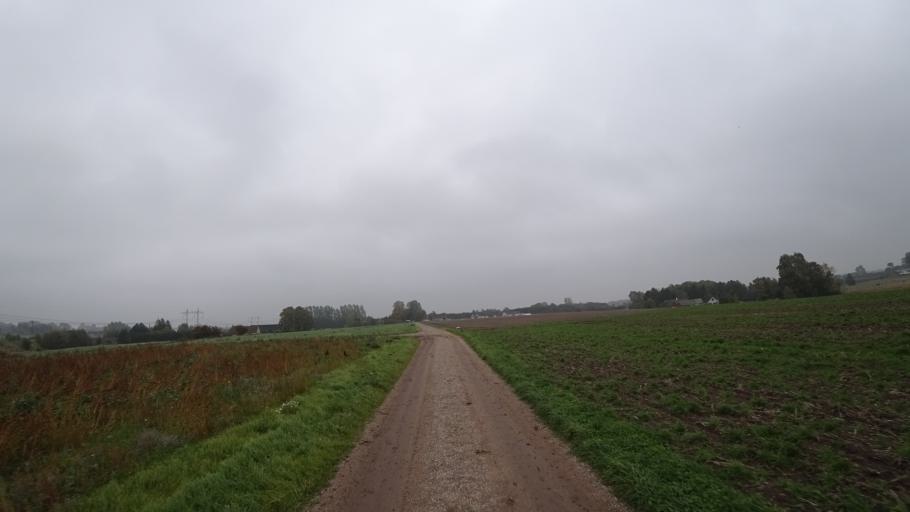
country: SE
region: Skane
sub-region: Kavlinge Kommun
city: Kaevlinge
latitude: 55.8154
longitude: 13.0820
